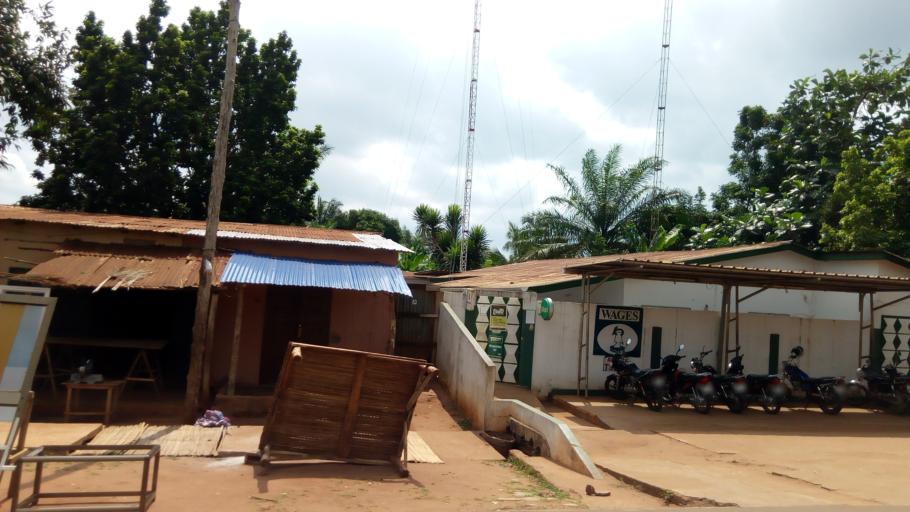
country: TG
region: Maritime
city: Tsevie
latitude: 6.4369
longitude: 1.2113
